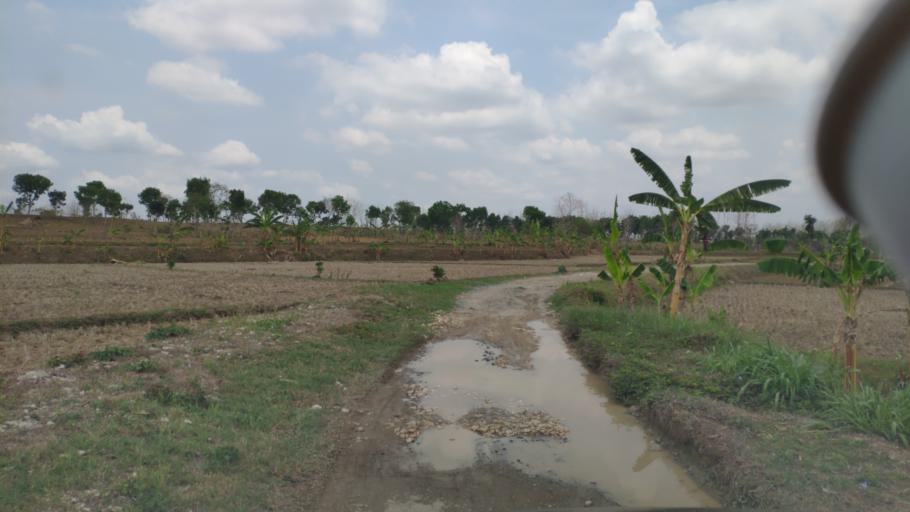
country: ID
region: Central Java
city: Gumiring
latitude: -7.0478
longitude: 111.3918
